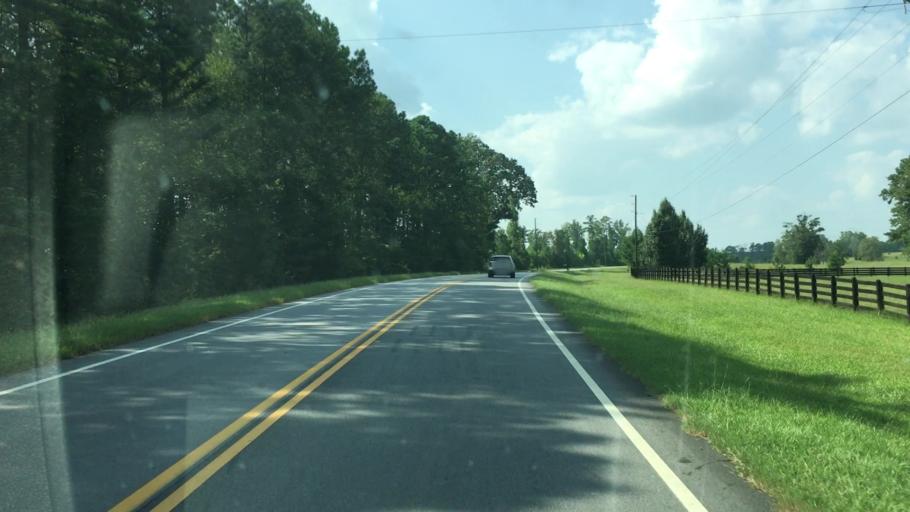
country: US
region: Georgia
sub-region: Jasper County
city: Monticello
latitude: 33.3302
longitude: -83.7090
